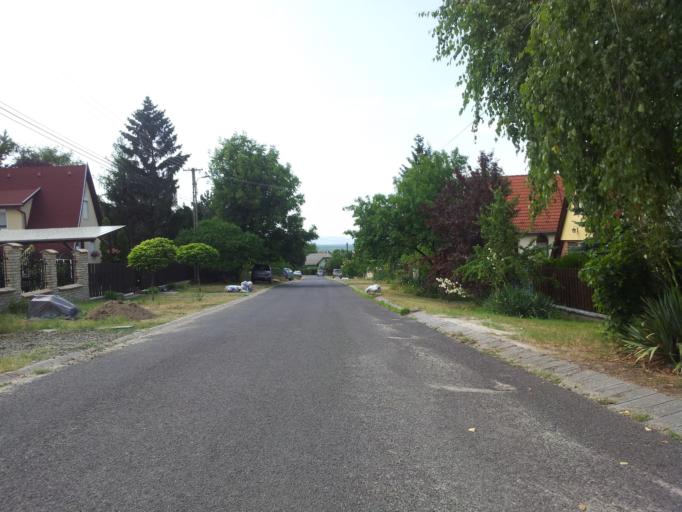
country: HU
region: Pest
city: Veresegyhaz
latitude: 47.6498
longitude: 19.3068
